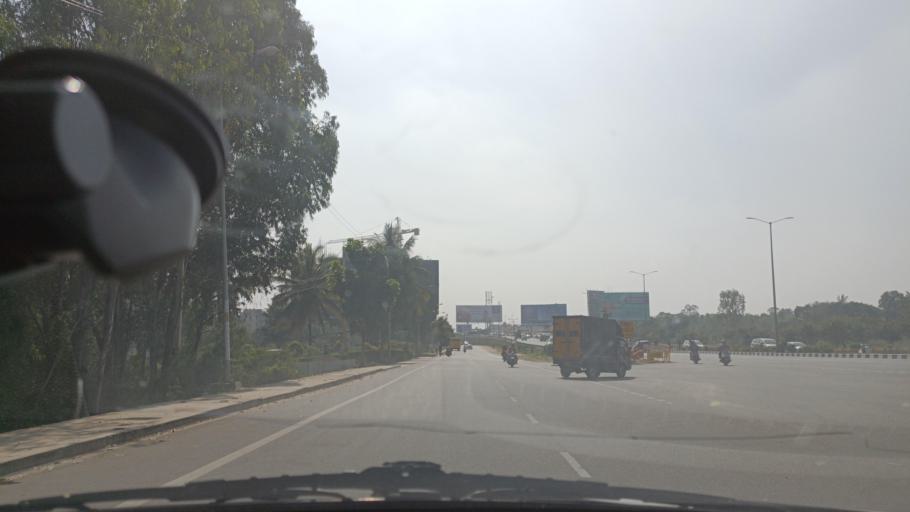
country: IN
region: Karnataka
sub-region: Bangalore Urban
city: Yelahanka
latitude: 13.1501
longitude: 77.6196
